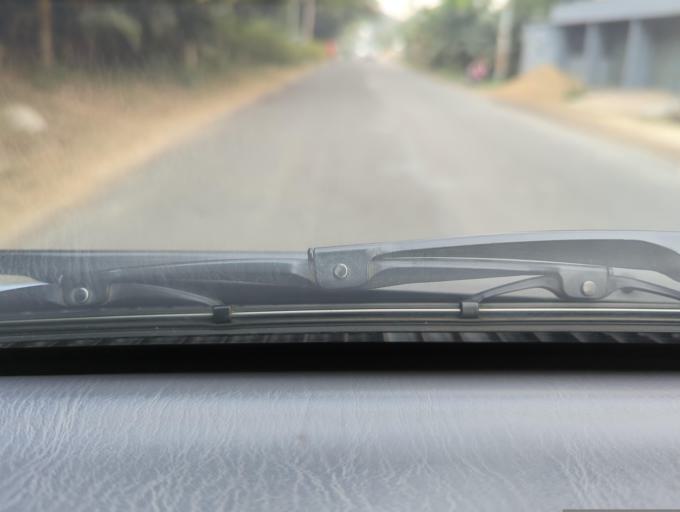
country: BD
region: Sylhet
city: Maulavi Bazar
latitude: 24.5082
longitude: 91.7305
